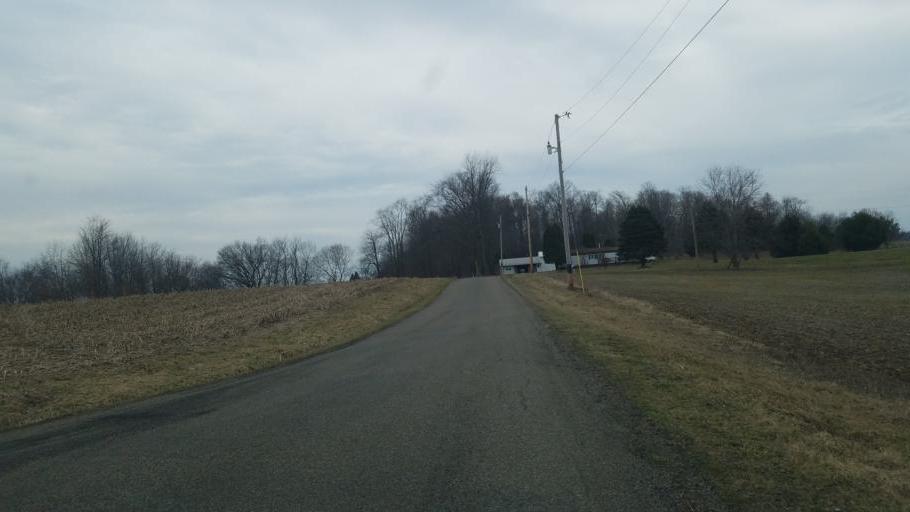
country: US
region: Ohio
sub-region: Ashland County
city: Loudonville
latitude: 40.7047
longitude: -82.3071
